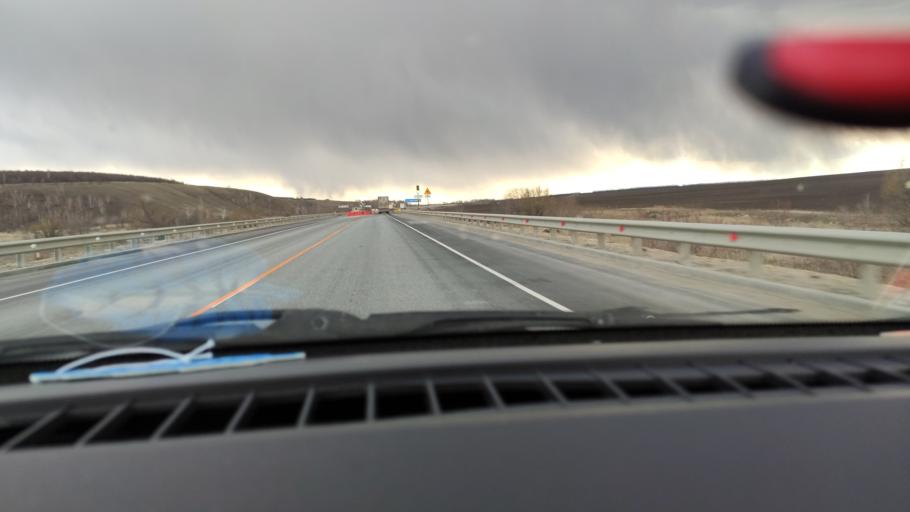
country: RU
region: Saratov
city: Yelshanka
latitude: 51.8641
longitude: 46.5012
